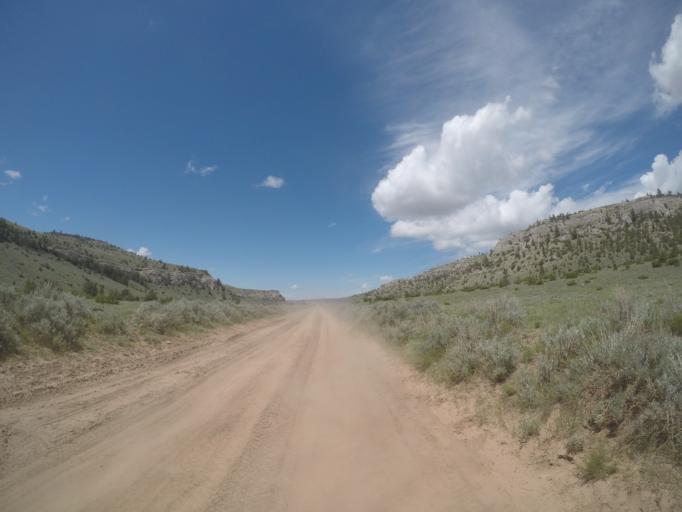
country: US
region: Wyoming
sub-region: Big Horn County
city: Lovell
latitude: 45.2314
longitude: -108.6096
